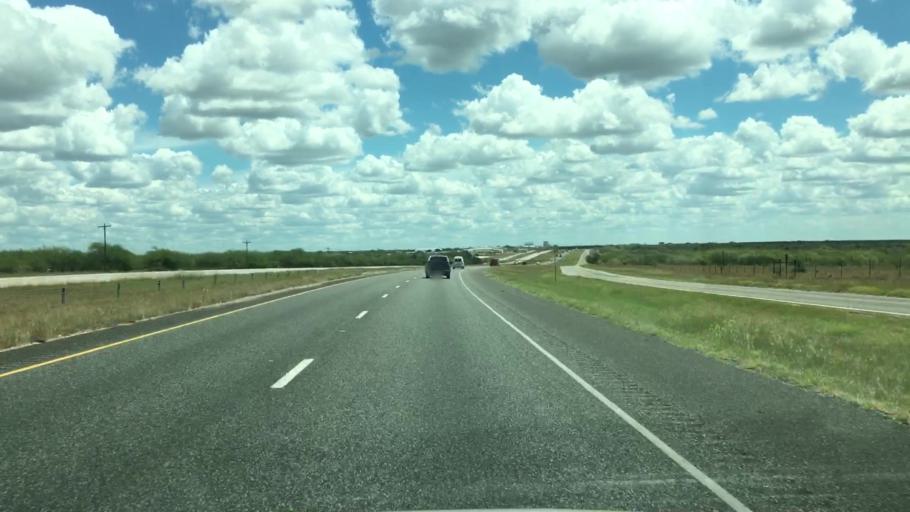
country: US
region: Texas
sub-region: Atascosa County
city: Pleasanton
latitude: 28.8999
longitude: -98.4203
